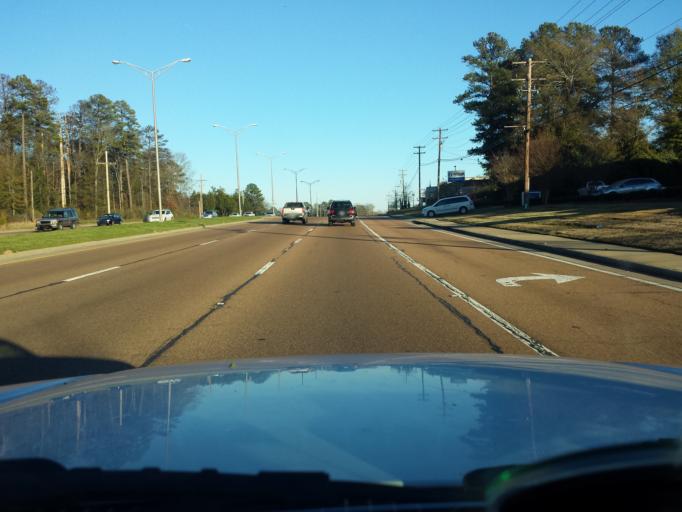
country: US
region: Mississippi
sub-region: Rankin County
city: Flowood
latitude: 32.3341
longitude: -90.1468
